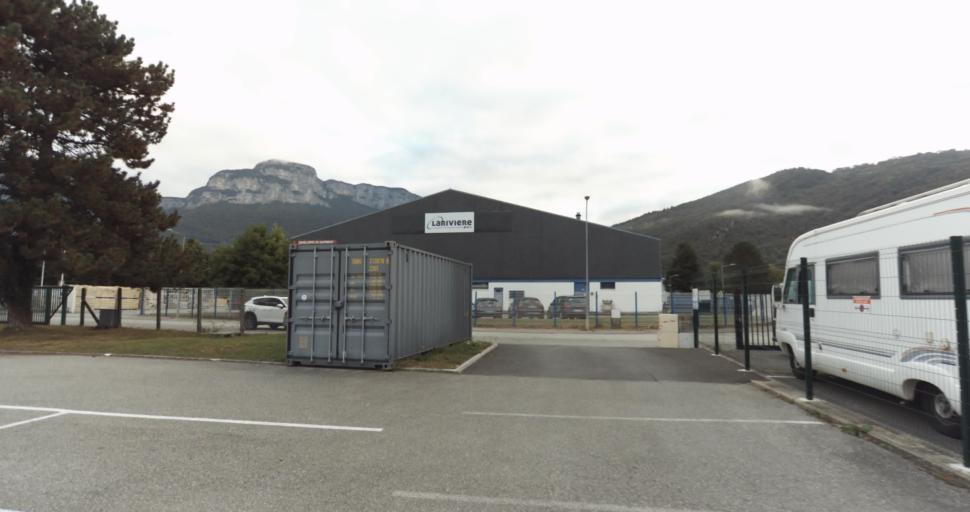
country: FR
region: Rhone-Alpes
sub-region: Departement de la Savoie
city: La Ravoire
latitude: 45.5664
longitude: 5.9713
